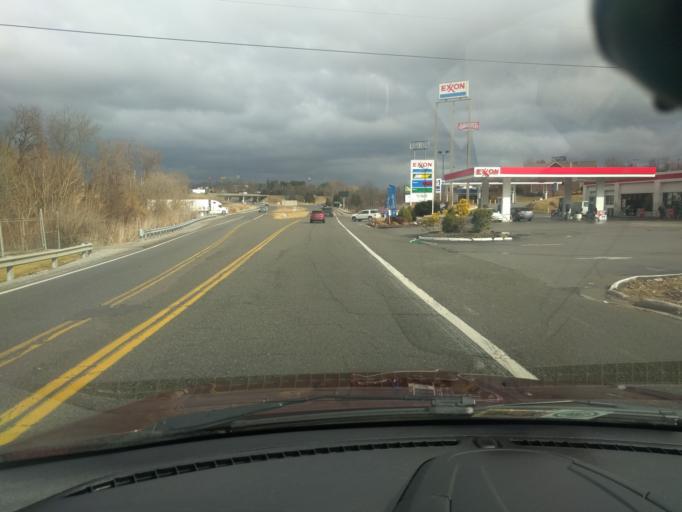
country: US
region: Virginia
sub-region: Pulaski County
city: Dublin
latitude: 37.0748
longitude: -80.6945
